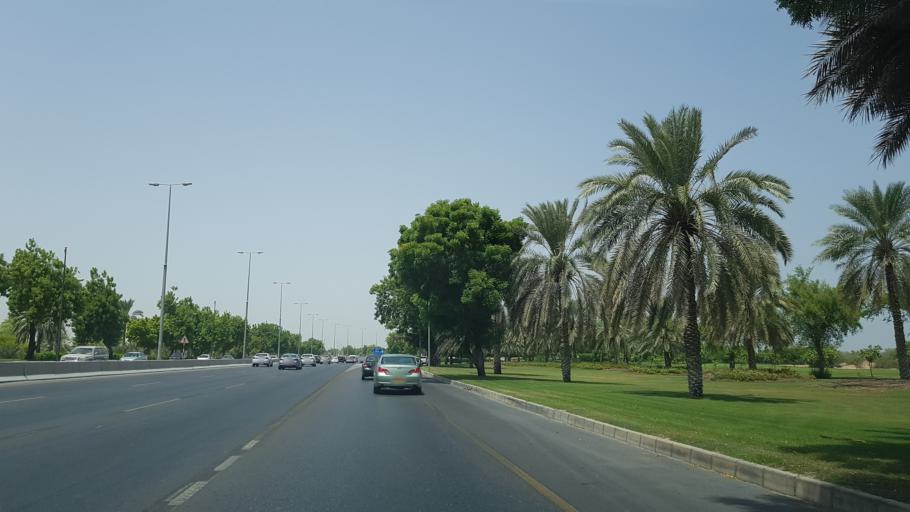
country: OM
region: Muhafazat Masqat
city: As Sib al Jadidah
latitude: 23.5840
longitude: 58.2612
